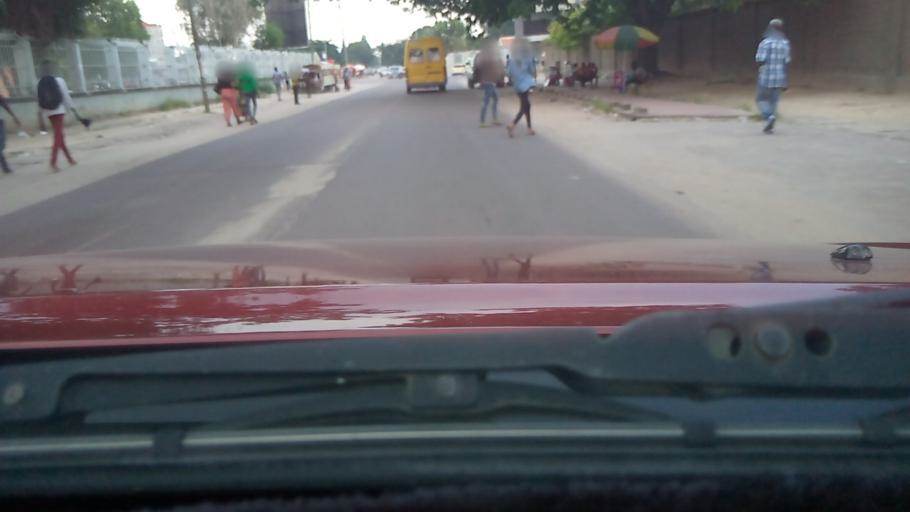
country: CD
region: Kinshasa
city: Kinshasa
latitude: -4.3076
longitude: 15.2854
